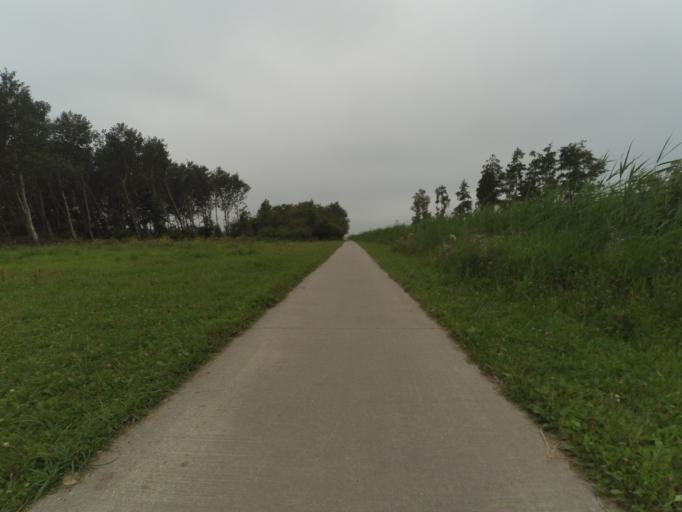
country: NL
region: Flevoland
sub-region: Gemeente Almere
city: Almere Stad
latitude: 52.4308
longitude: 5.2623
